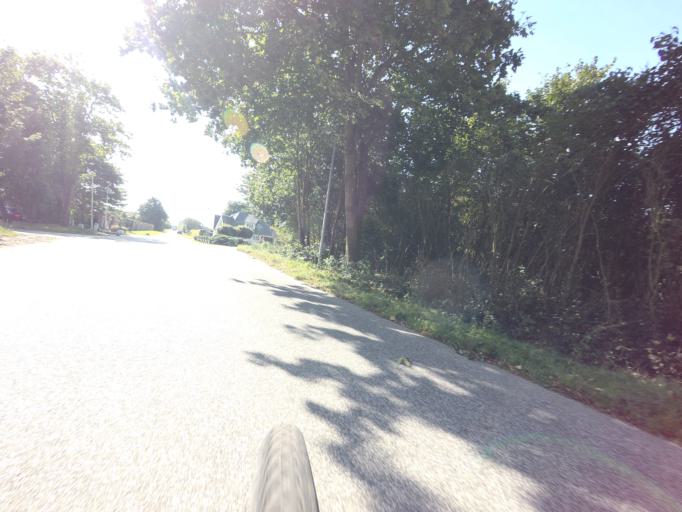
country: DK
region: Central Jutland
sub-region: Viborg Kommune
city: Viborg
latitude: 56.4228
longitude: 9.3818
